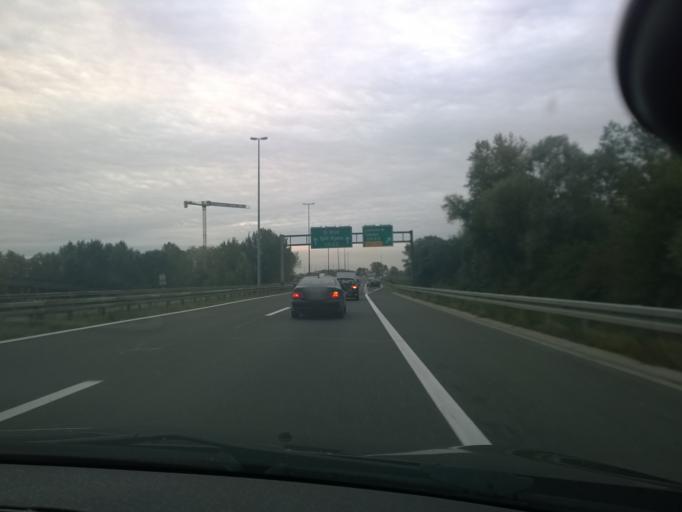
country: HR
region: Grad Zagreb
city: Jezdovec
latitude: 45.7933
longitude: 15.8463
